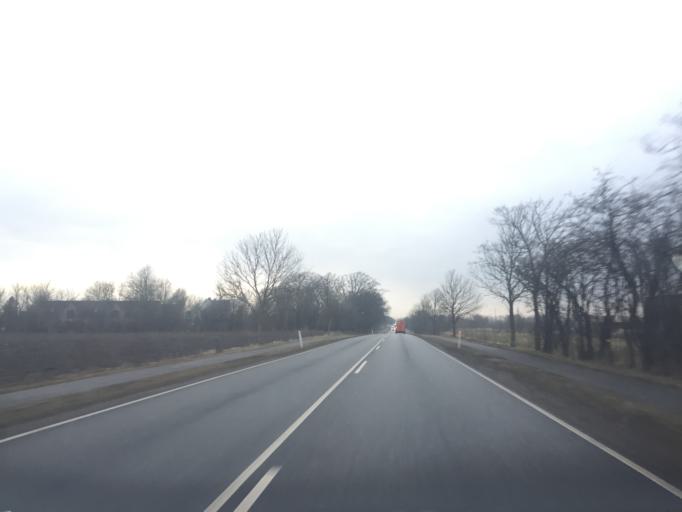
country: DK
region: Zealand
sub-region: Solrod Kommune
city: Solrod Strand
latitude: 55.5831
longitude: 12.2409
